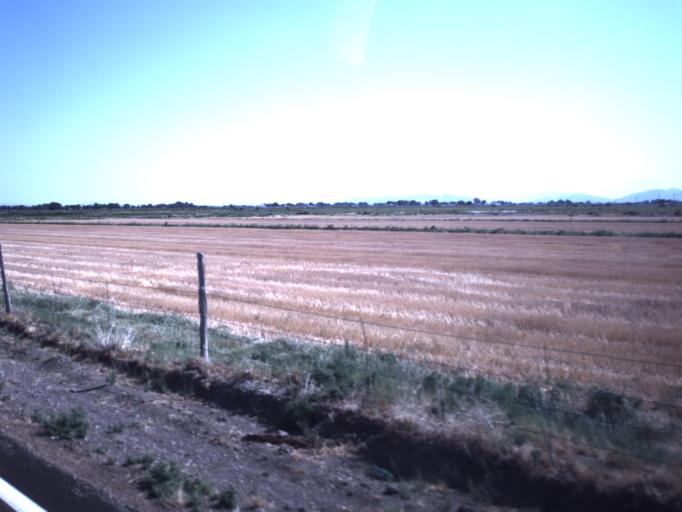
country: US
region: Utah
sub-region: Millard County
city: Delta
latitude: 39.2662
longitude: -112.6531
